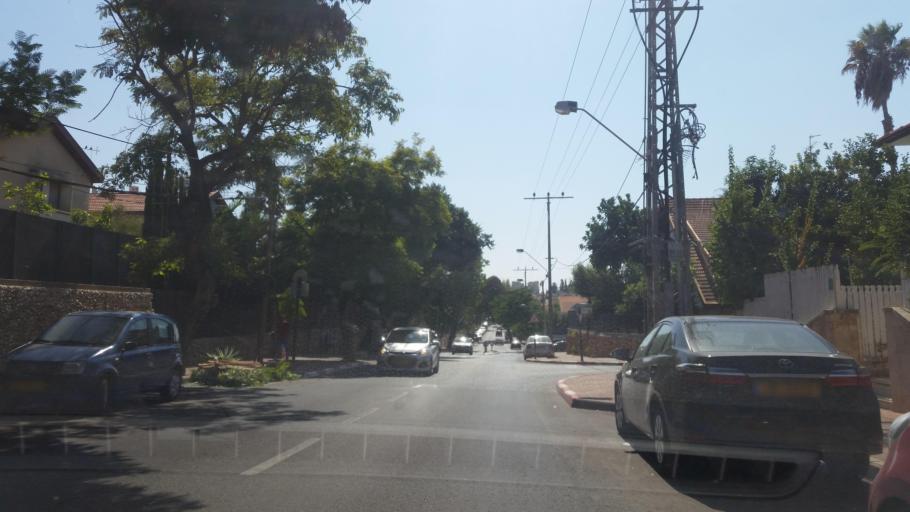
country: IL
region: Central District
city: Ra'anana
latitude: 32.1845
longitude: 34.8863
